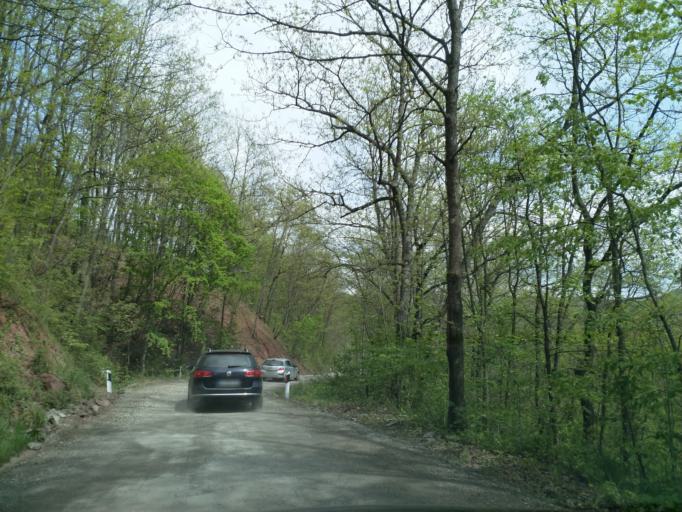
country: RS
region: Central Serbia
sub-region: Pomoravski Okrug
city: Despotovac
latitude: 43.9553
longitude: 21.5741
